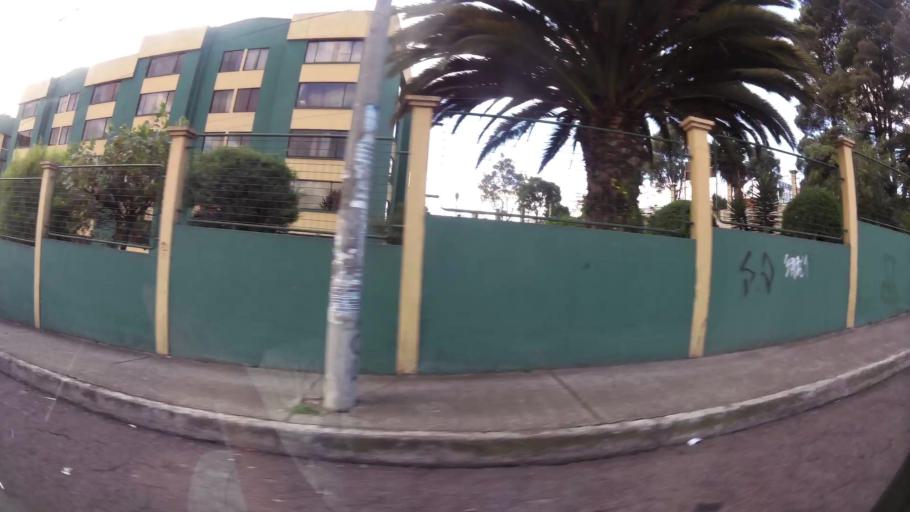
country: EC
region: Pichincha
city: Quito
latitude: -0.1312
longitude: -78.4761
